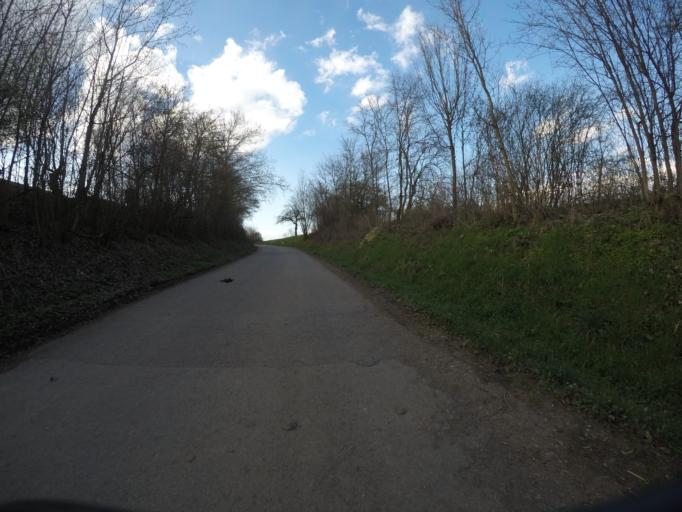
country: DE
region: Baden-Wuerttemberg
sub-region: Tuebingen Region
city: Ofterdingen
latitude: 48.4267
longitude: 9.0306
